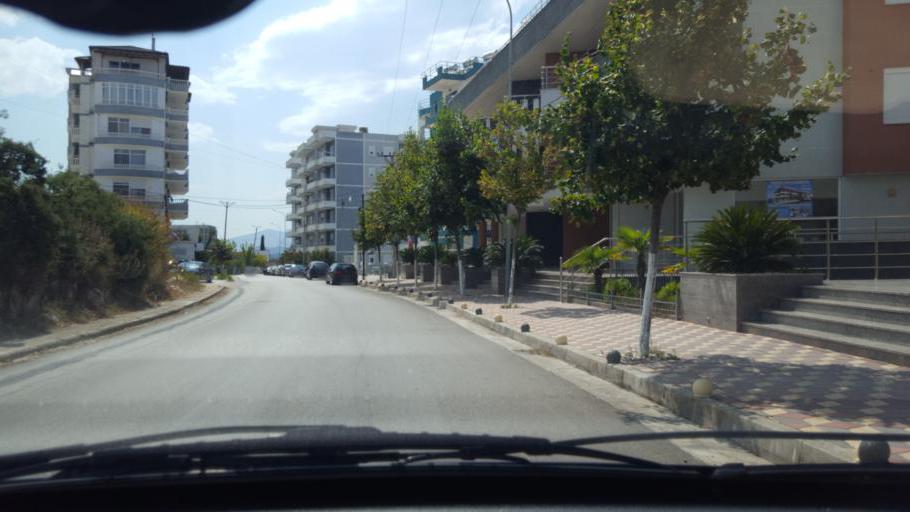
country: AL
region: Vlore
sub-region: Rrethi i Sarandes
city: Sarande
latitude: 39.8500
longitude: 20.0225
